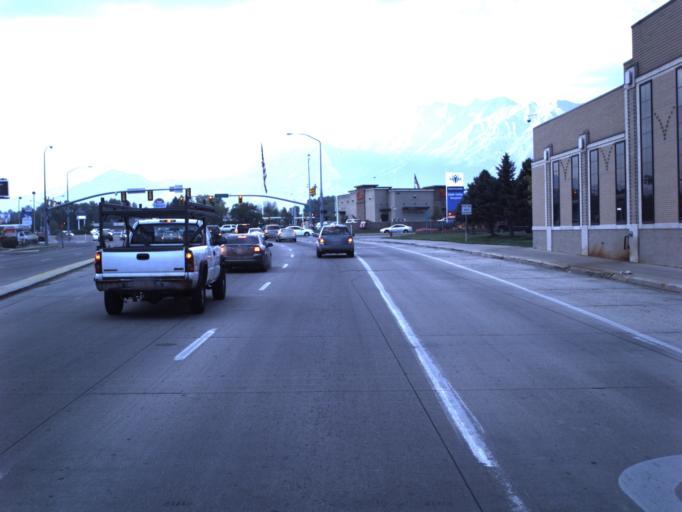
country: US
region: Utah
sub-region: Utah County
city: Provo
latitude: 40.2495
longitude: -111.6673
